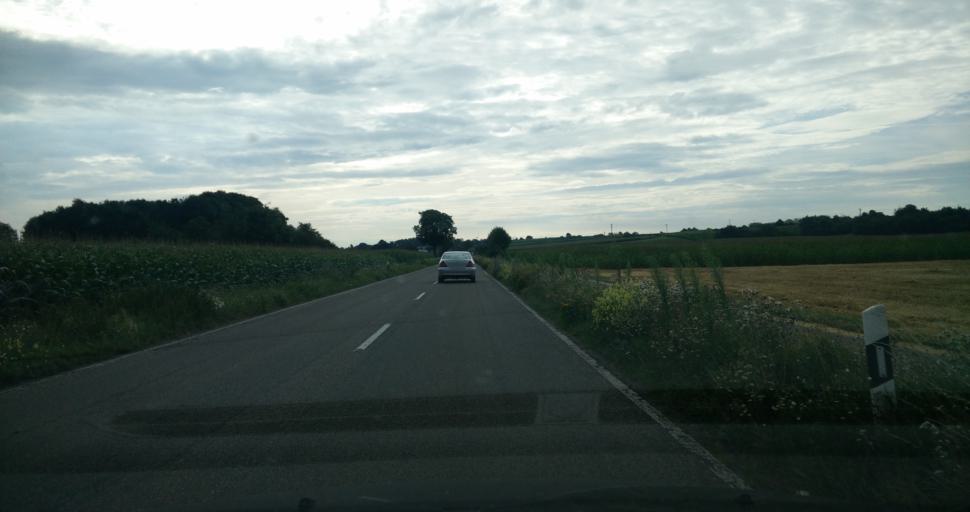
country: DE
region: Rheinland-Pfalz
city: Barbelroth
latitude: 49.0975
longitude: 8.0711
